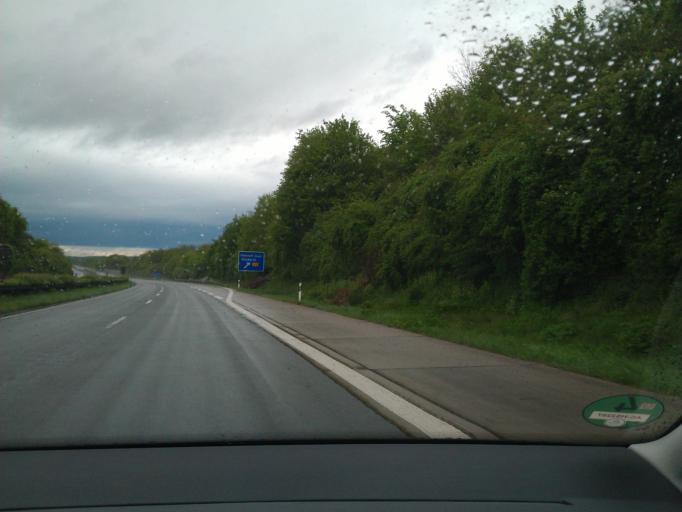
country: DE
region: North Rhine-Westphalia
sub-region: Regierungsbezirk Koln
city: Hennef
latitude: 50.7734
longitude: 7.3052
